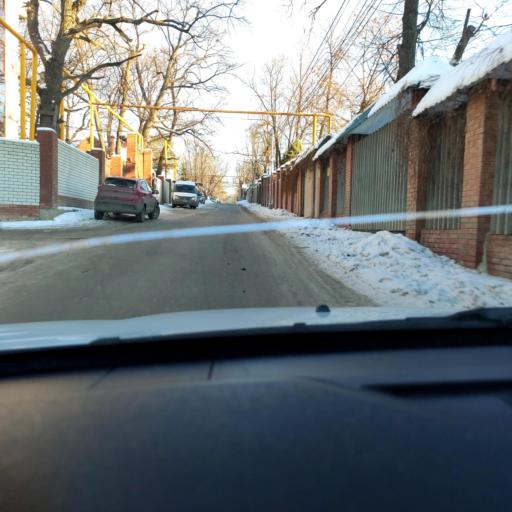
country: RU
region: Samara
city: Samara
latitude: 53.2623
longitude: 50.1893
